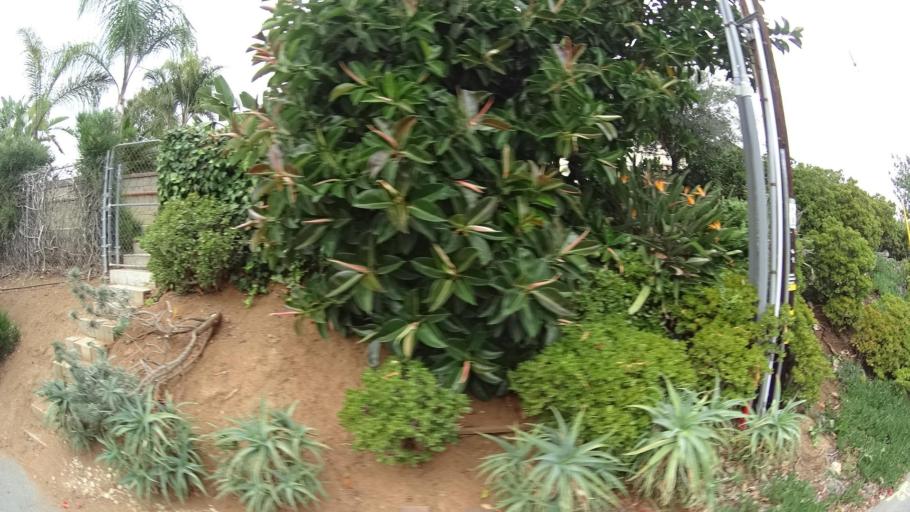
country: US
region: California
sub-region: San Diego County
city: Spring Valley
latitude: 32.7555
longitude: -116.9912
